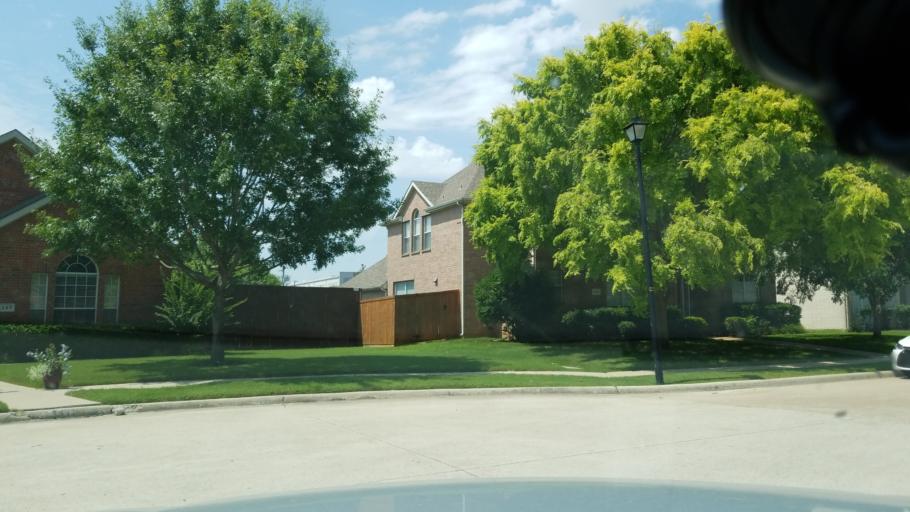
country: US
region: Texas
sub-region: Dallas County
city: Coppell
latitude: 32.9659
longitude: -96.9875
